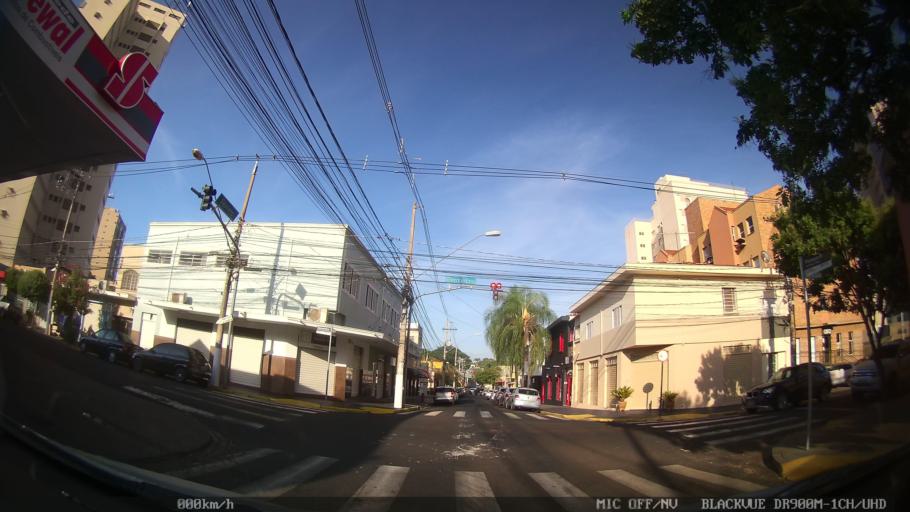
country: BR
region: Sao Paulo
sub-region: Ribeirao Preto
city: Ribeirao Preto
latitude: -21.1863
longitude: -47.8069
